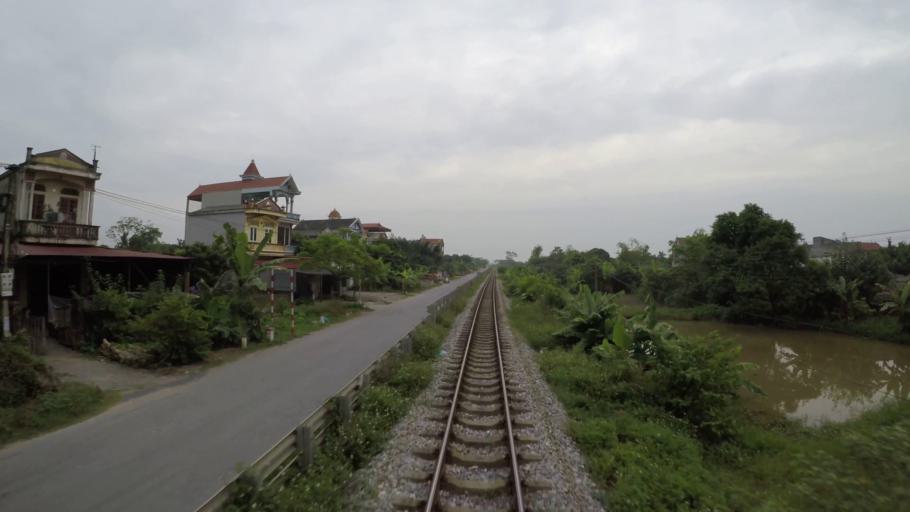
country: VN
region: Hung Yen
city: Ban Yen Nhan
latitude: 20.9658
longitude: 106.1104
